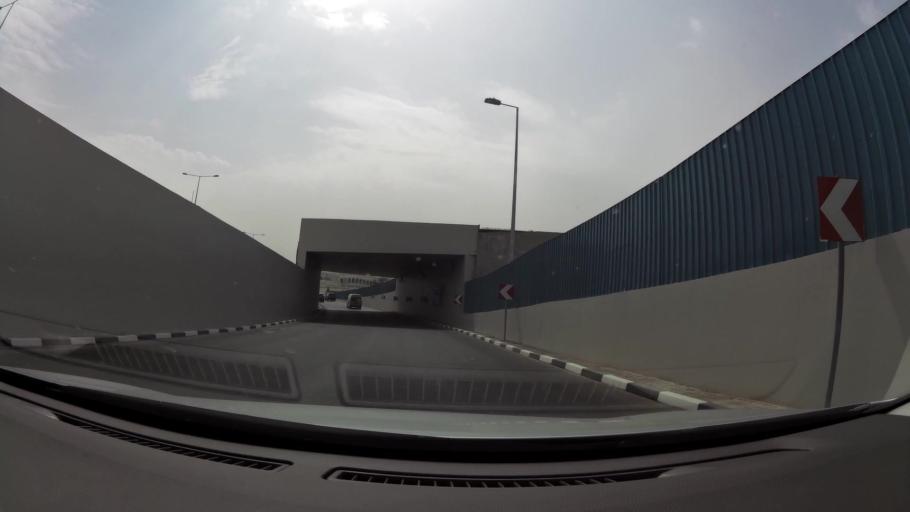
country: QA
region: Baladiyat ad Dawhah
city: Doha
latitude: 25.2964
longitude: 51.5155
